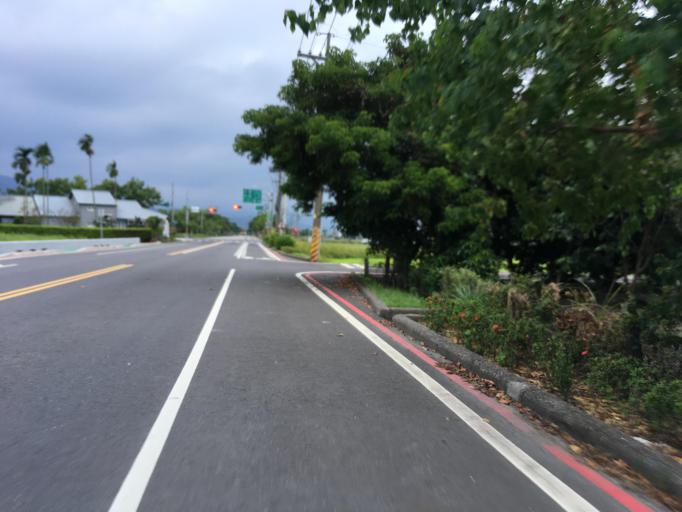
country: TW
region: Taiwan
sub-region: Yilan
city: Yilan
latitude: 24.6805
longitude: 121.6887
